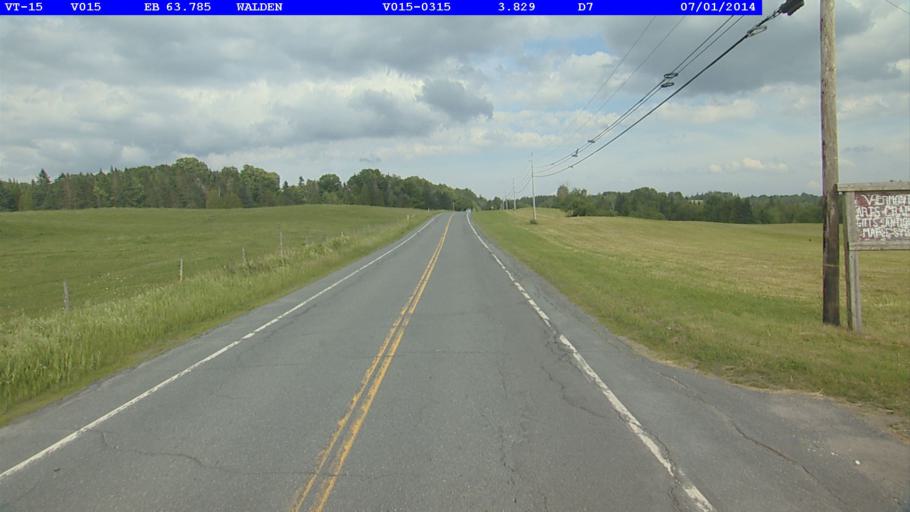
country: US
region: Vermont
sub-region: Caledonia County
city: Hardwick
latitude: 44.4492
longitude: -72.2508
